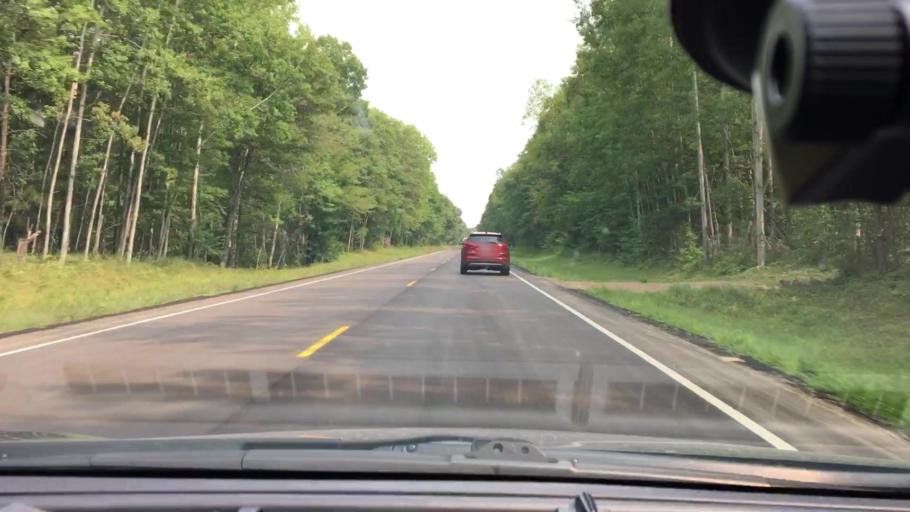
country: US
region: Minnesota
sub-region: Crow Wing County
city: Breezy Point
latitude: 46.5336
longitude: -94.1711
